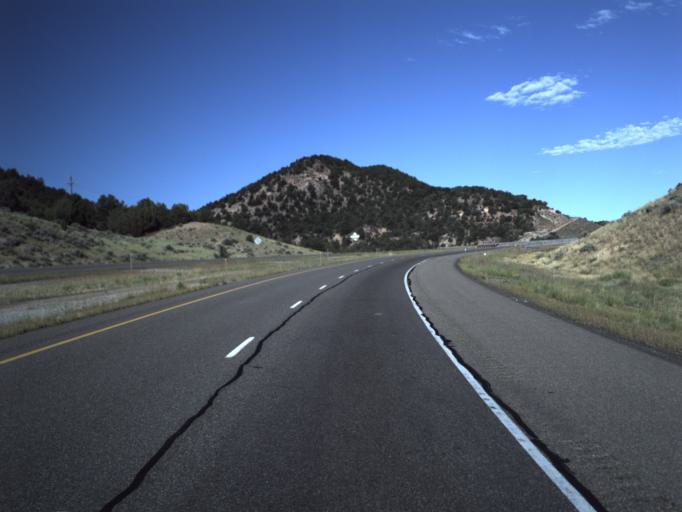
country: US
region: Utah
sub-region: Sevier County
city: Monroe
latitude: 38.5472
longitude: -112.3760
